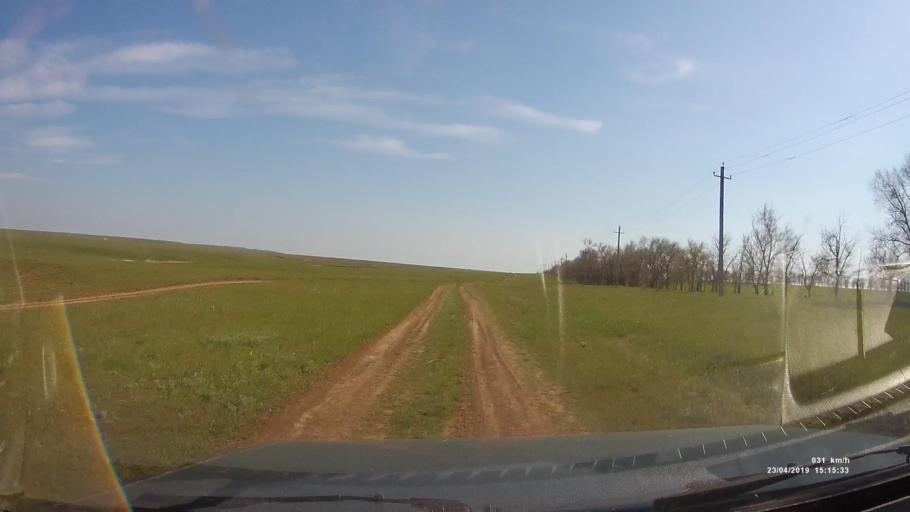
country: RU
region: Rostov
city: Remontnoye
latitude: 46.5381
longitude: 42.9698
